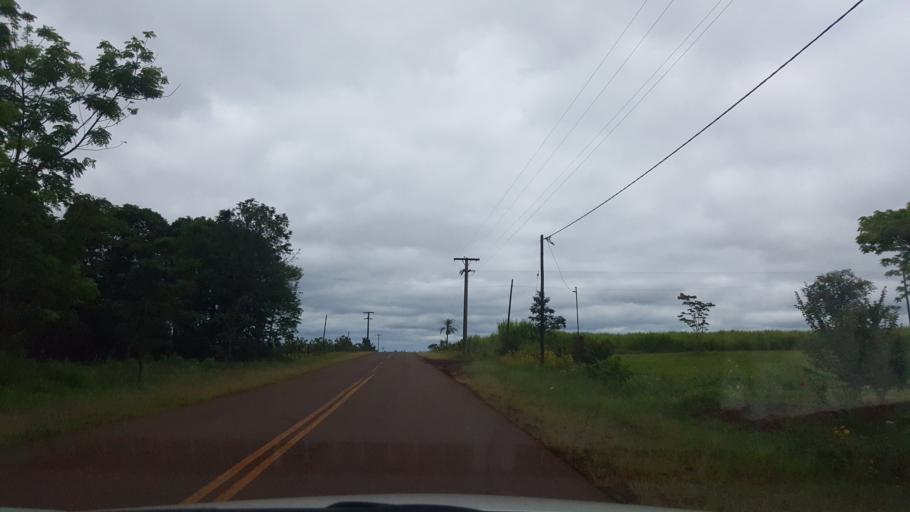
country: AR
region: Misiones
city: Ruiz de Montoya
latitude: -26.9686
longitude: -55.0626
